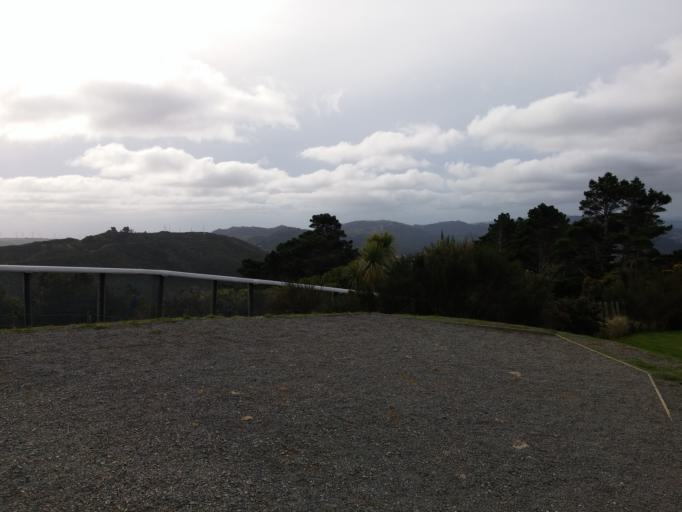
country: NZ
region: Wellington
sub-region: Wellington City
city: Brooklyn
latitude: -41.3109
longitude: 174.7453
